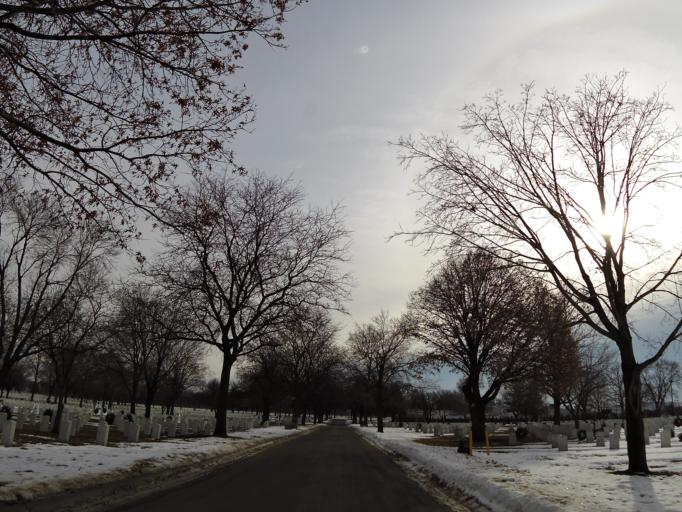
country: US
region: Minnesota
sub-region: Hennepin County
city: Richfield
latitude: 44.8747
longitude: -93.2221
